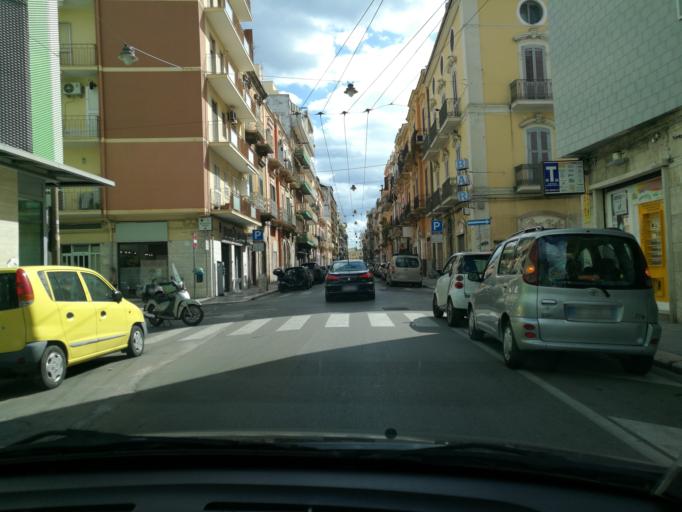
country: IT
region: Apulia
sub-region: Provincia di Bari
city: Bari
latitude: 41.1269
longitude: 16.8581
